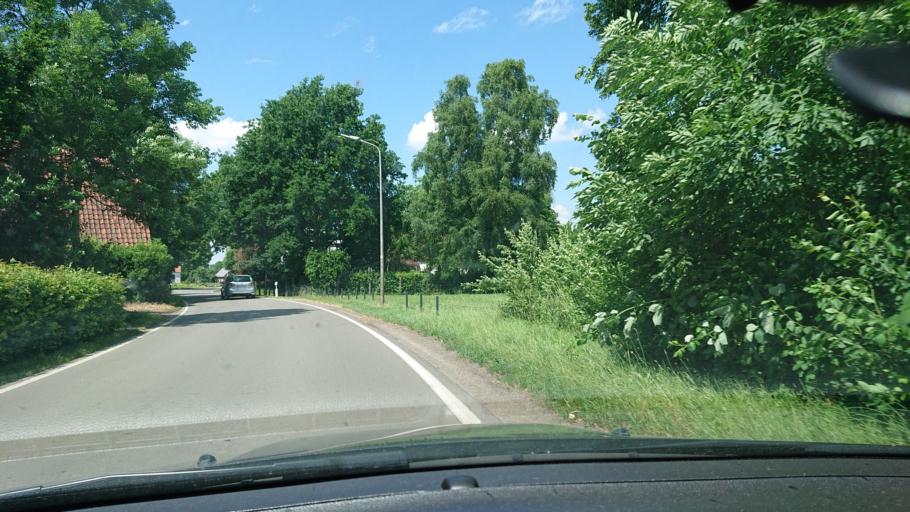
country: DE
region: North Rhine-Westphalia
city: Preussisch Oldendorf
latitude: 52.3139
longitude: 8.4847
